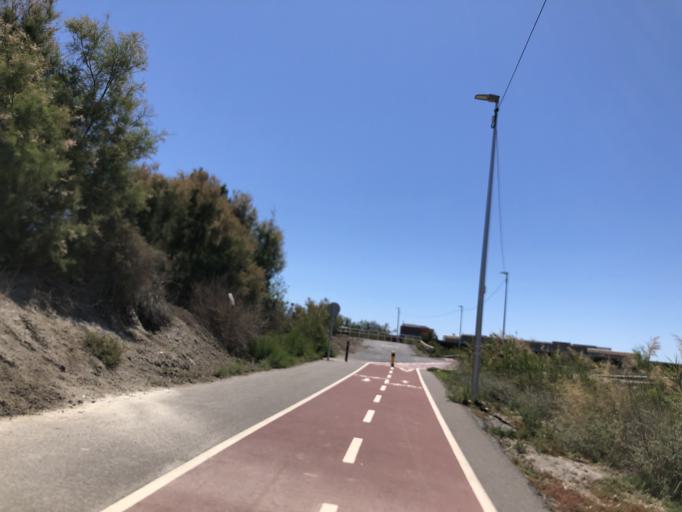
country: ES
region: Andalusia
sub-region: Provincia de Almeria
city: Almeria
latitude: 36.8334
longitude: -2.4026
